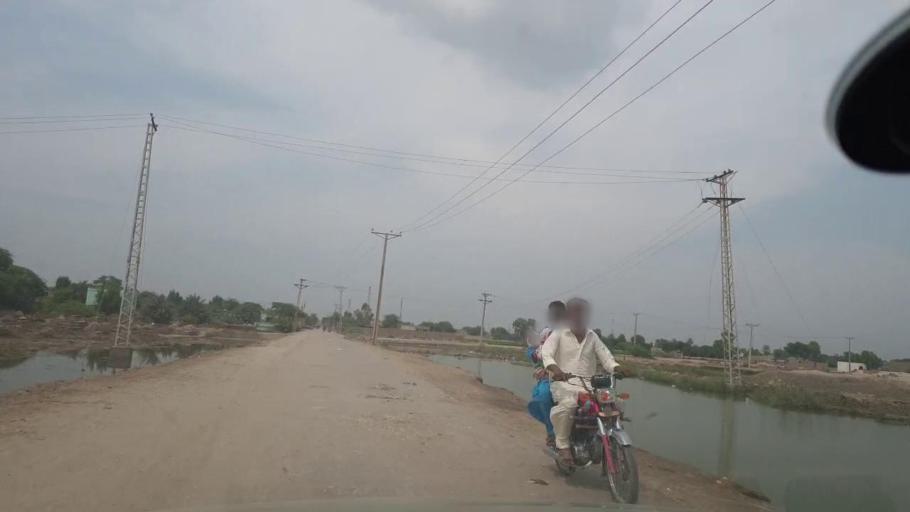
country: PK
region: Sindh
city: Jacobabad
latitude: 28.2615
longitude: 68.4374
